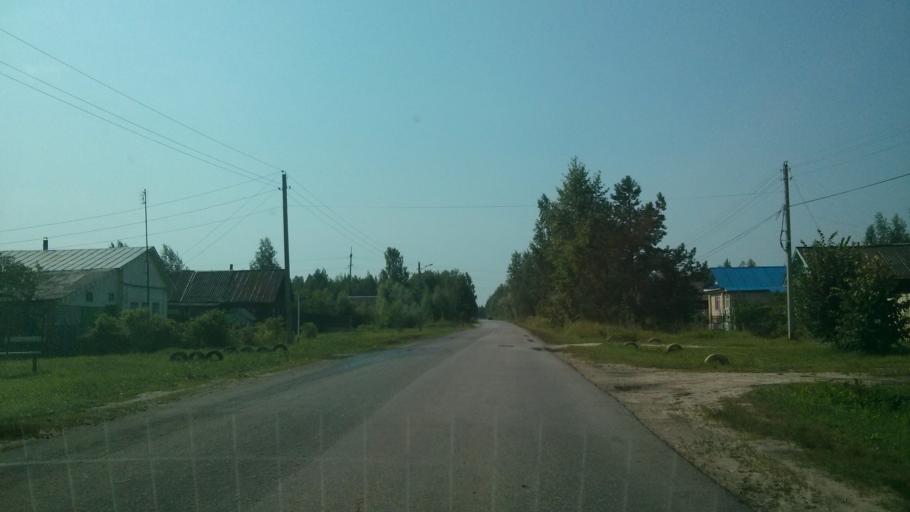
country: RU
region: Vladimir
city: Murom
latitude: 55.5338
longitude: 42.0240
